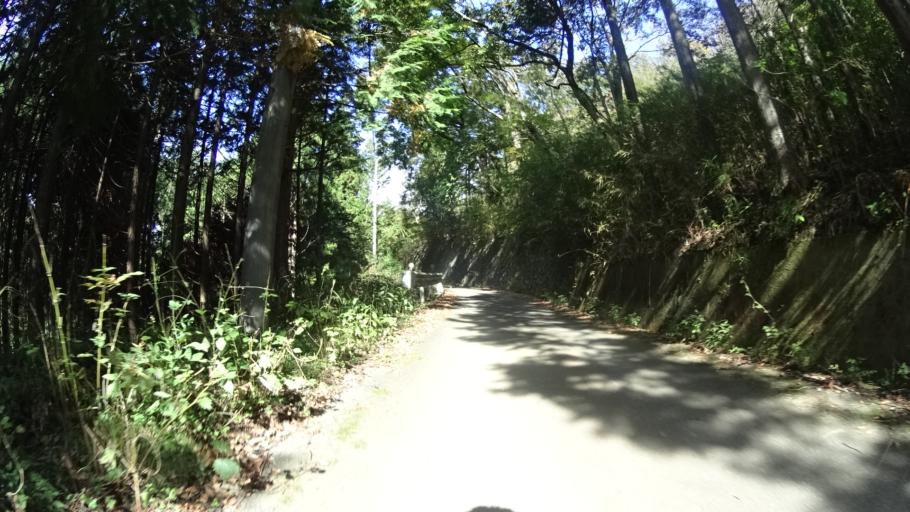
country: JP
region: Yamanashi
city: Otsuki
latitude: 35.5825
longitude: 138.9719
